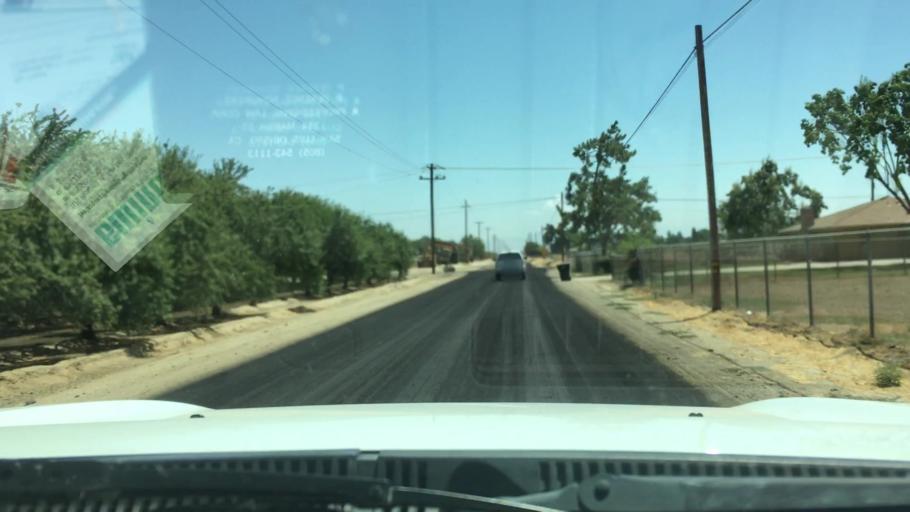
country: US
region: California
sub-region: Kern County
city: Shafter
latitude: 35.5291
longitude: -119.3145
